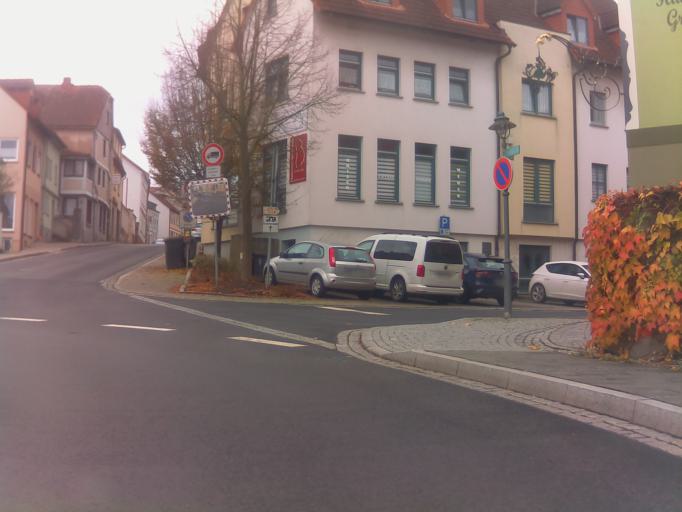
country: DE
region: Thuringia
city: Geisa
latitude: 50.7169
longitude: 9.9499
